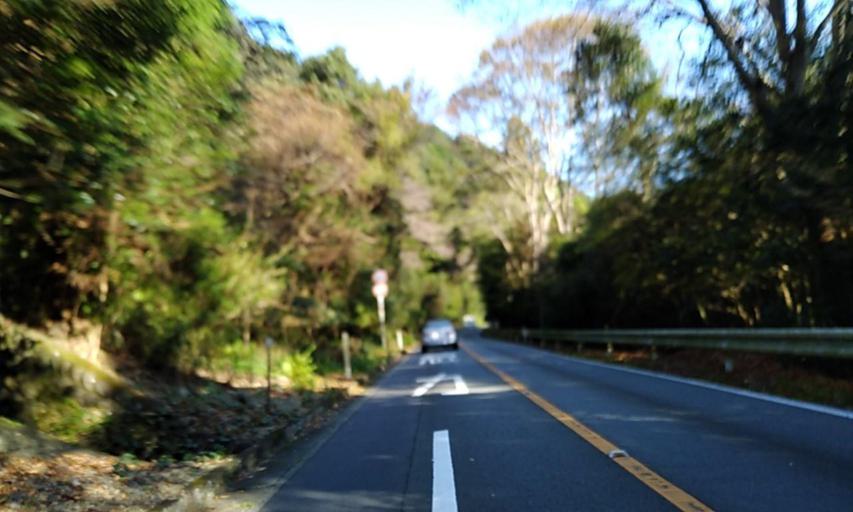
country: JP
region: Mie
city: Ise
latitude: 34.4420
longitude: 136.7524
